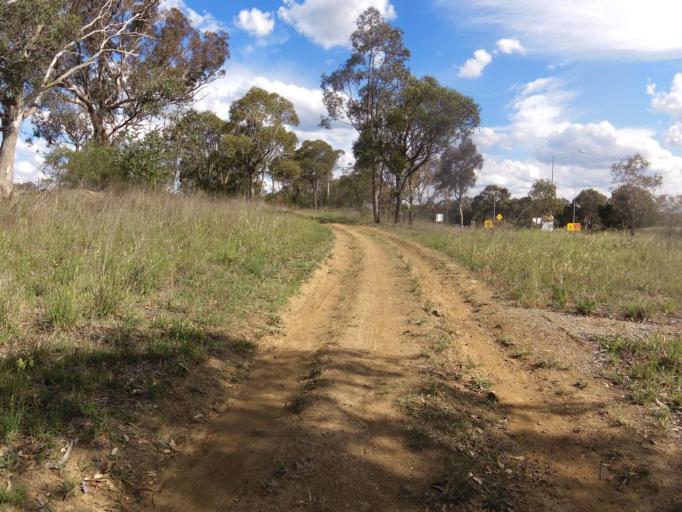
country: AU
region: Australian Capital Territory
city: Belconnen
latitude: -35.1811
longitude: 149.0742
